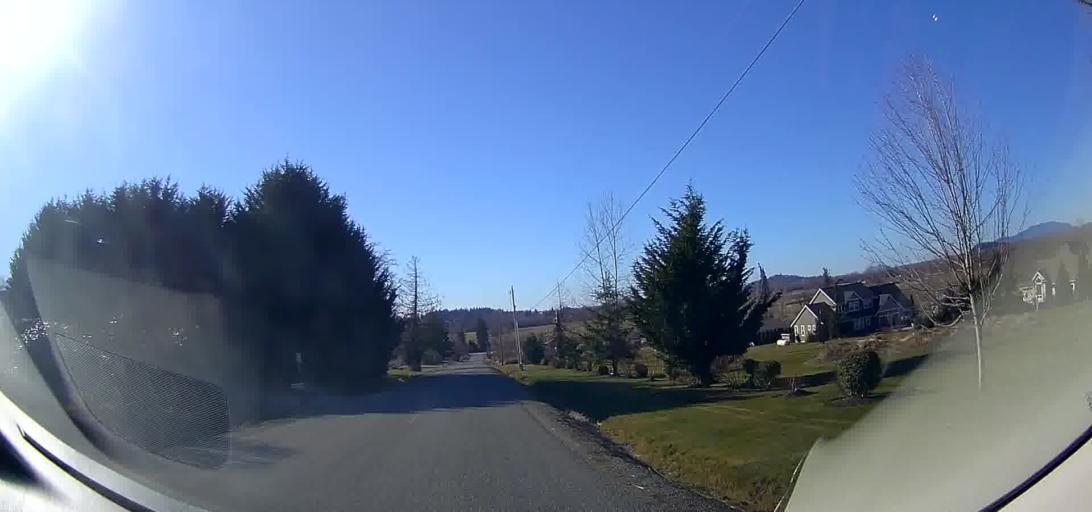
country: US
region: Washington
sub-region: Skagit County
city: Clear Lake
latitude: 48.4570
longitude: -122.2534
